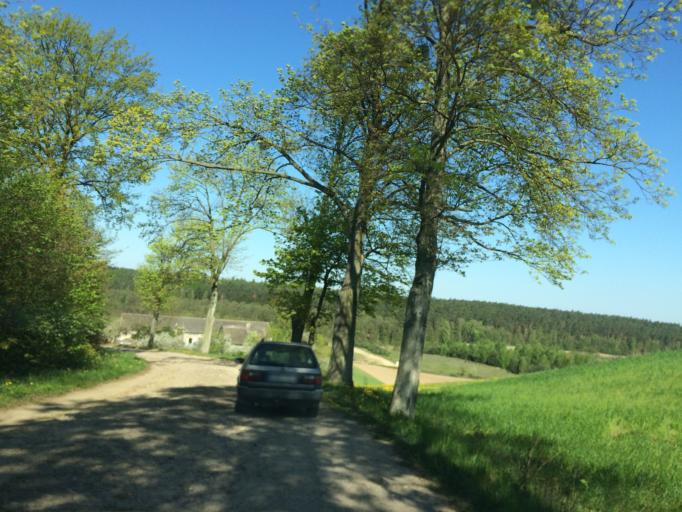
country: PL
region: Warmian-Masurian Voivodeship
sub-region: Powiat nowomiejski
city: Biskupiec
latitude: 53.4873
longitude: 19.4784
